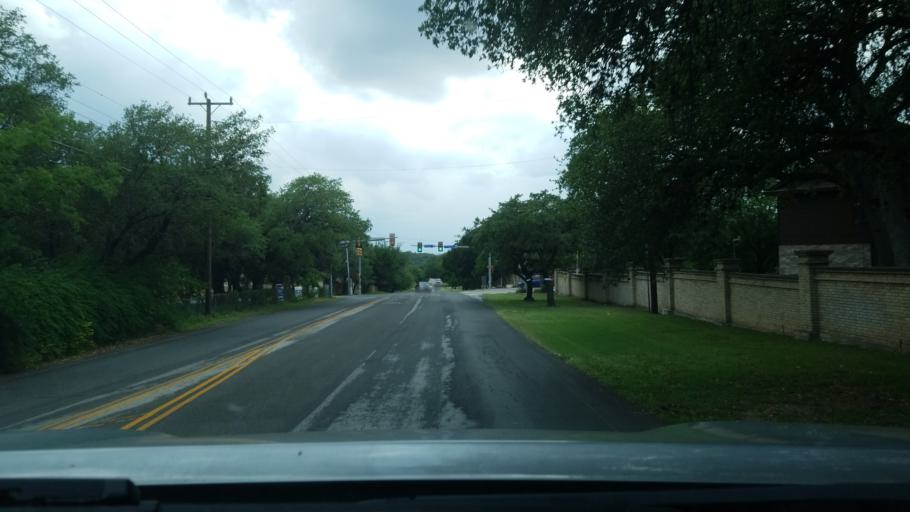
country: US
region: Texas
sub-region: Bexar County
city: Leon Valley
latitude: 29.5448
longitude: -98.5992
